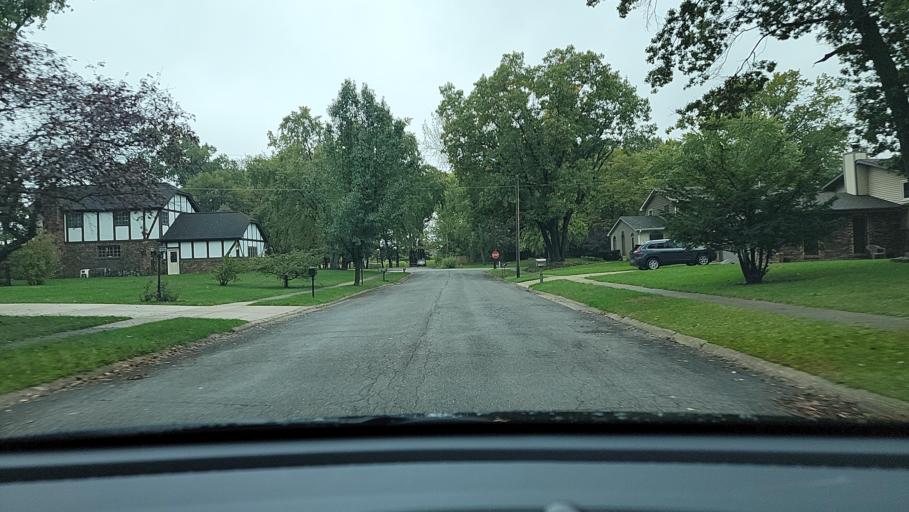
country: US
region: Indiana
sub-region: Porter County
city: Portage
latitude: 41.5694
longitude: -87.1763
